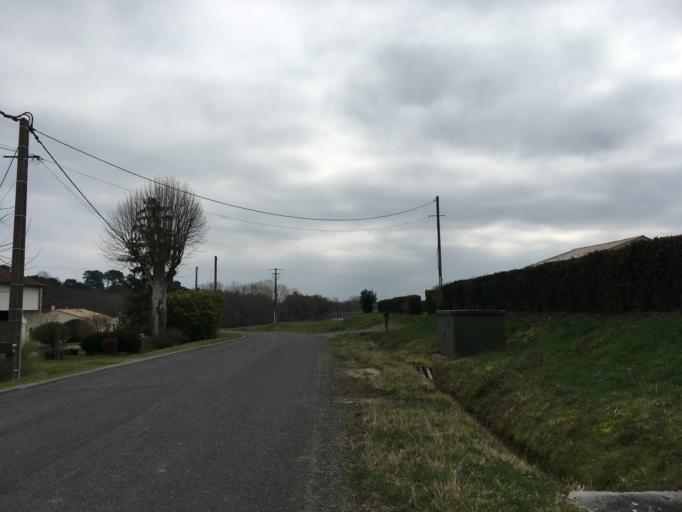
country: FR
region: Poitou-Charentes
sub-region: Departement de la Charente-Maritime
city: Mirambeau
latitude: 45.3302
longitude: -0.5870
